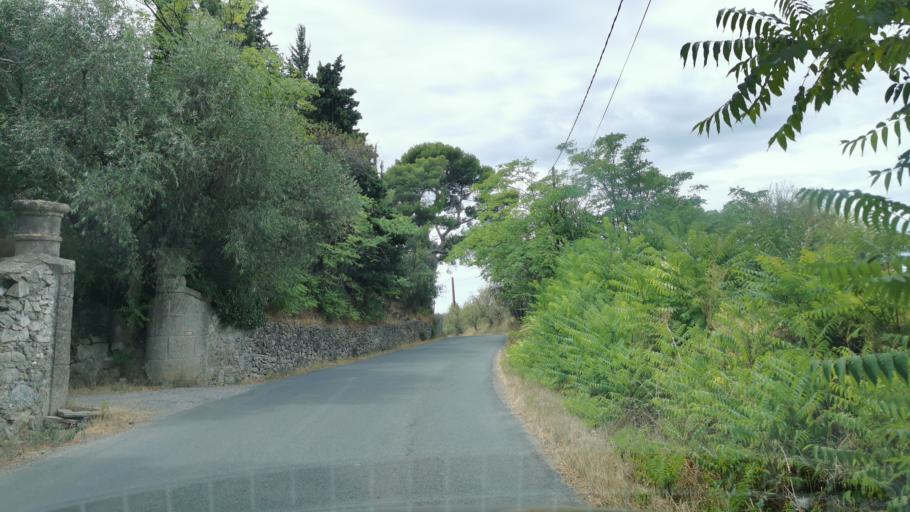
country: FR
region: Languedoc-Roussillon
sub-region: Departement de l'Aude
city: Ginestas
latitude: 43.2769
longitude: 2.8731
